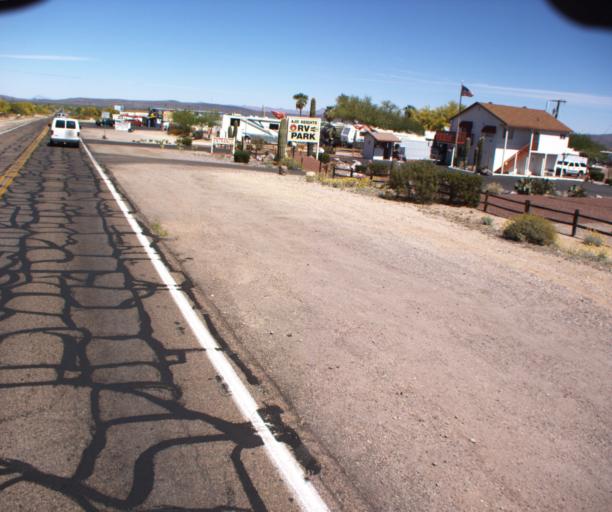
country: US
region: Arizona
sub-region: Pima County
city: Ajo
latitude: 32.3931
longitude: -112.8721
